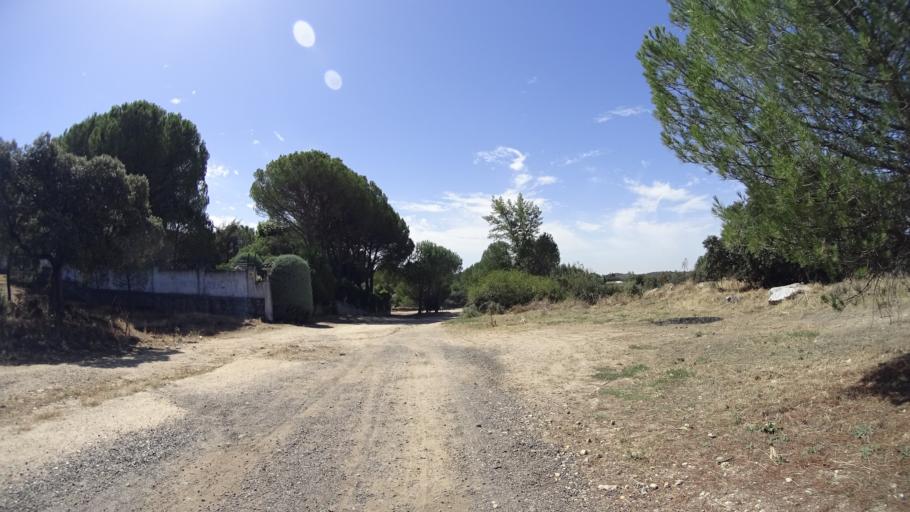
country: ES
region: Madrid
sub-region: Provincia de Madrid
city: Torrelodones
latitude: 40.5704
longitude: -3.9445
